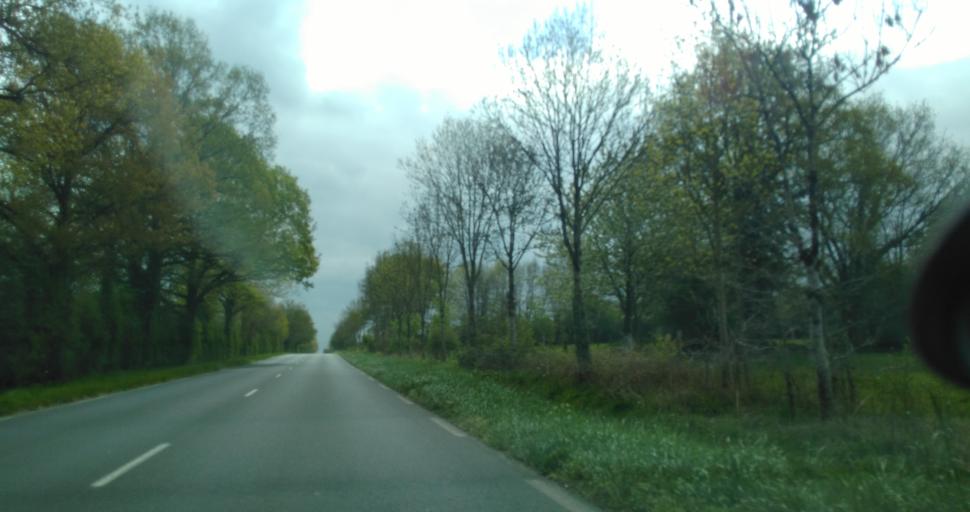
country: FR
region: Poitou-Charentes
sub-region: Departement des Deux-Sevres
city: Moncoutant
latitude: 46.7449
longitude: -0.6114
